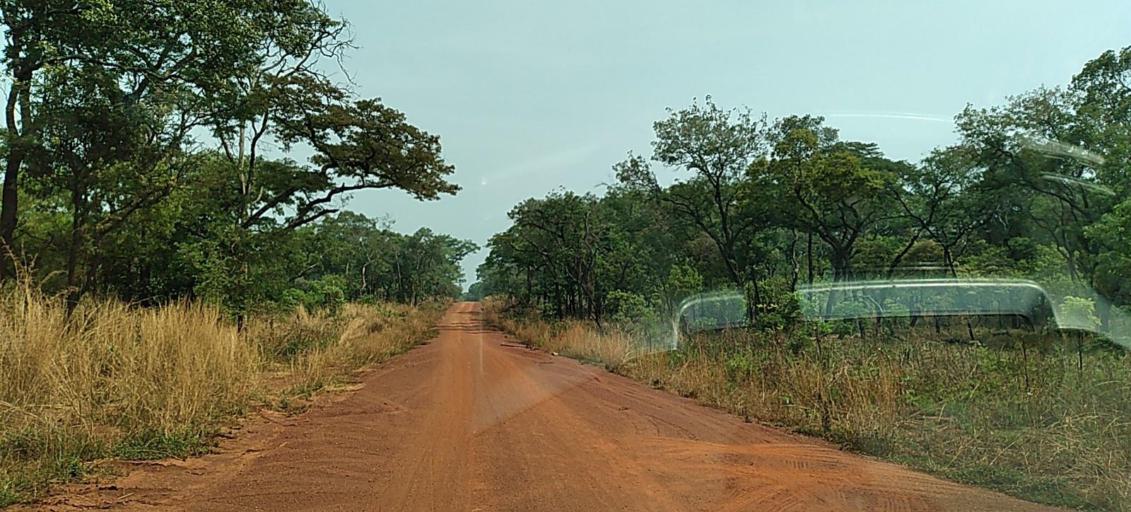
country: ZM
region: North-Western
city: Kansanshi
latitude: -11.9966
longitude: 26.8385
